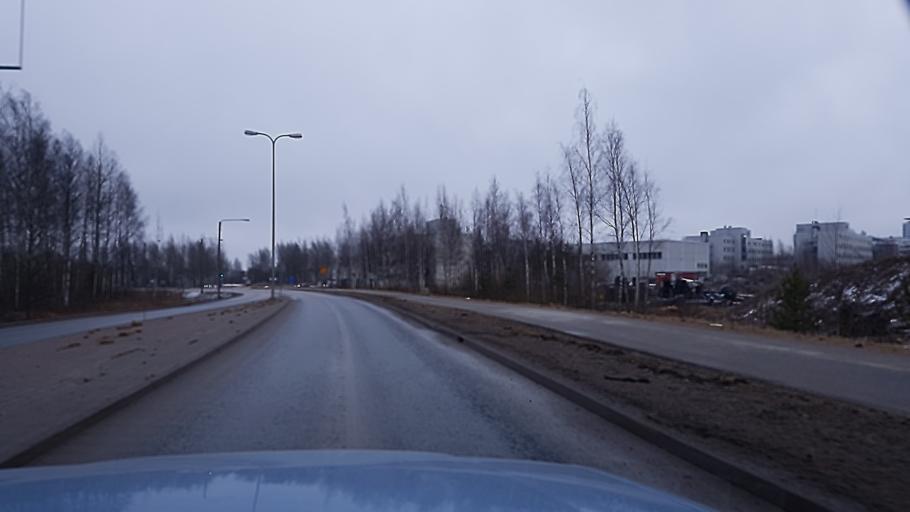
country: FI
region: Uusimaa
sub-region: Helsinki
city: Vantaa
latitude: 60.2979
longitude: 24.9703
